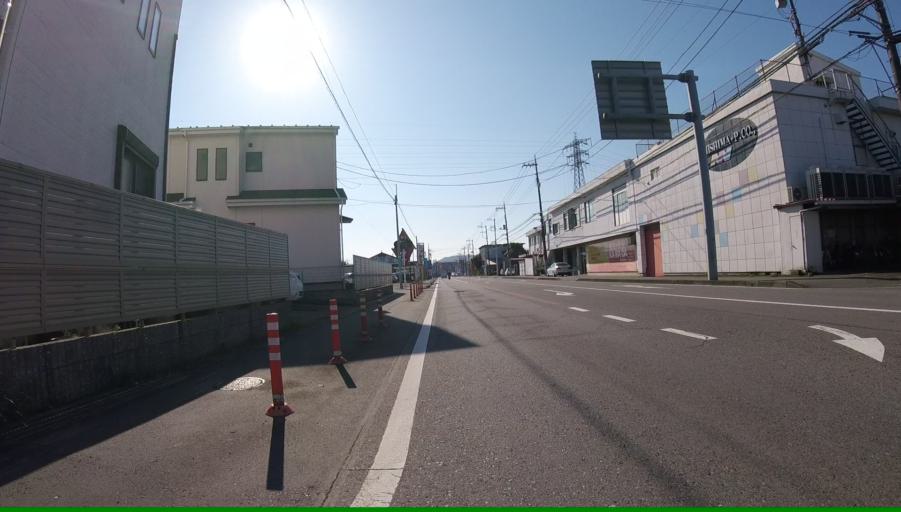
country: JP
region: Shizuoka
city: Mishima
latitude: 35.1072
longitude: 138.9158
